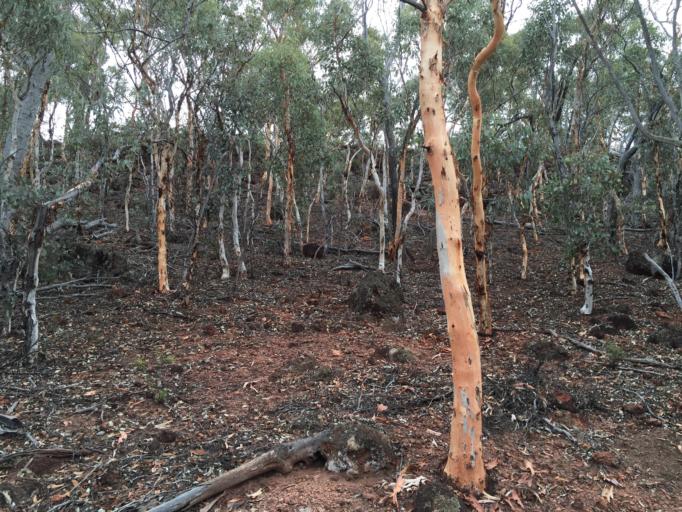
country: AU
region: Western Australia
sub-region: Narrogin
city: Narrogin
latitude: -32.7967
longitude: 116.9452
